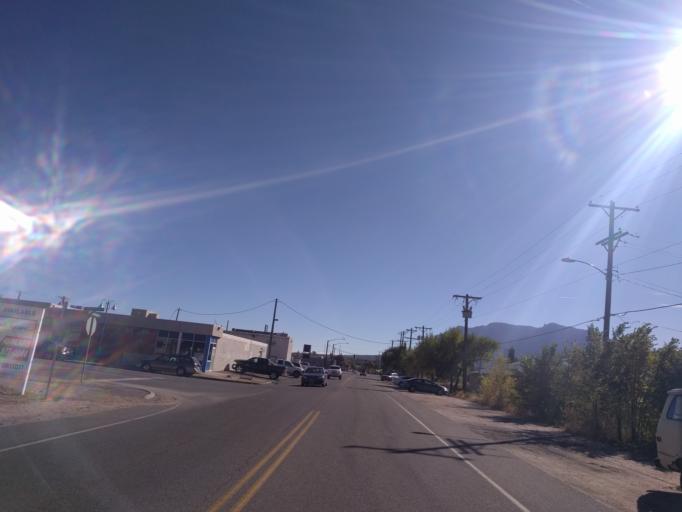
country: US
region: Colorado
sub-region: El Paso County
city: Colorado Springs
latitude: 38.8287
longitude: -104.8292
